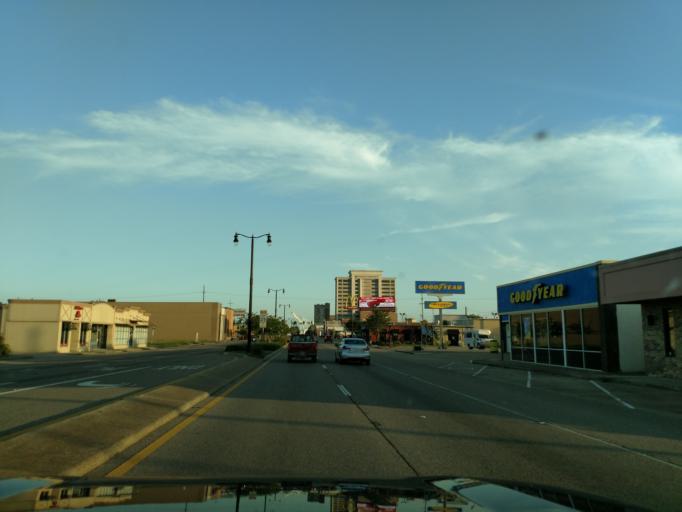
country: US
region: Mississippi
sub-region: Harrison County
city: Gulfport
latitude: 30.3733
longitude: -89.0930
